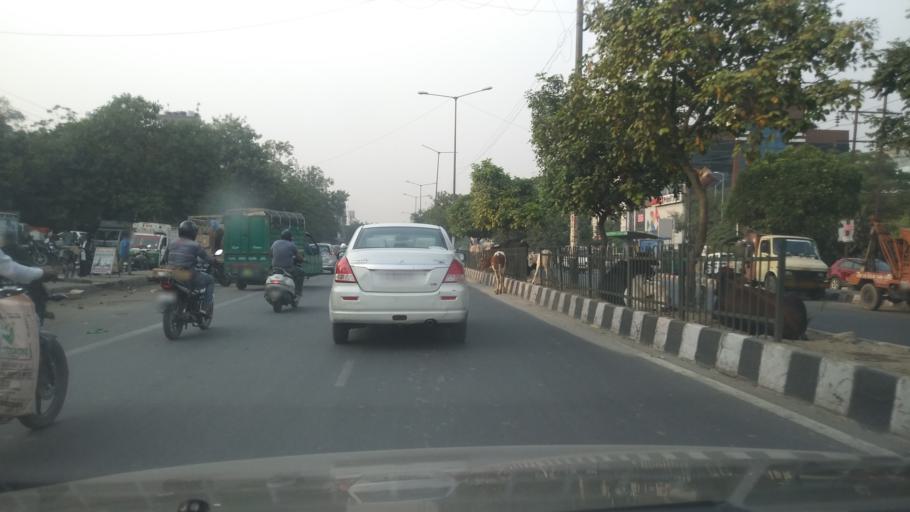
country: IN
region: Uttar Pradesh
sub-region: Gautam Buddha Nagar
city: Noida
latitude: 28.5335
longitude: 77.2687
